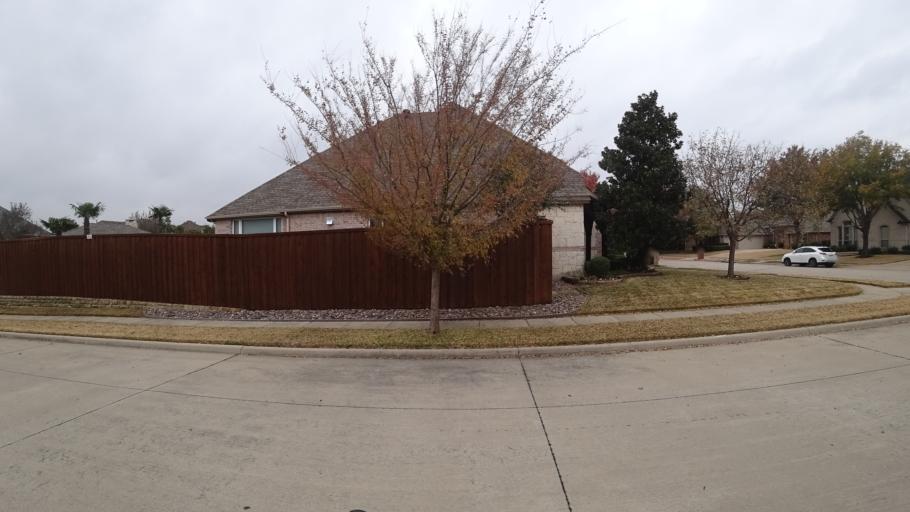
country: US
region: Texas
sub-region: Denton County
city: Lewisville
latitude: 33.0331
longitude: -96.9364
